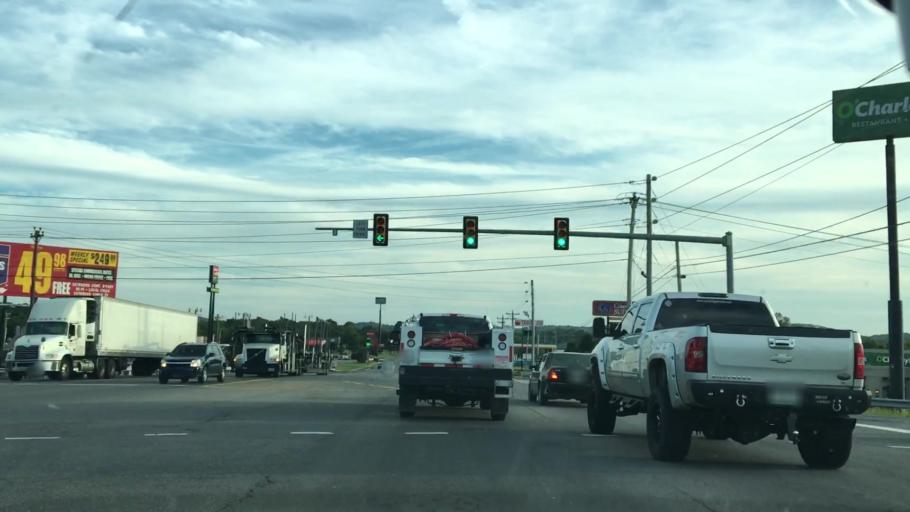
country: US
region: Tennessee
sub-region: Wilson County
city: Lebanon
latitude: 36.1816
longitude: -86.2994
